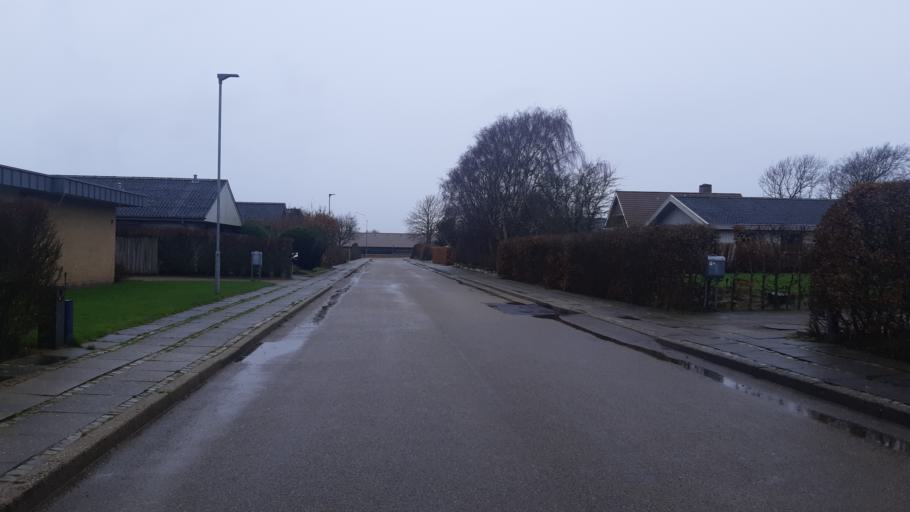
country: DK
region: Central Jutland
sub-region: Ringkobing-Skjern Kommune
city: Ringkobing
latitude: 56.0922
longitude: 8.2662
